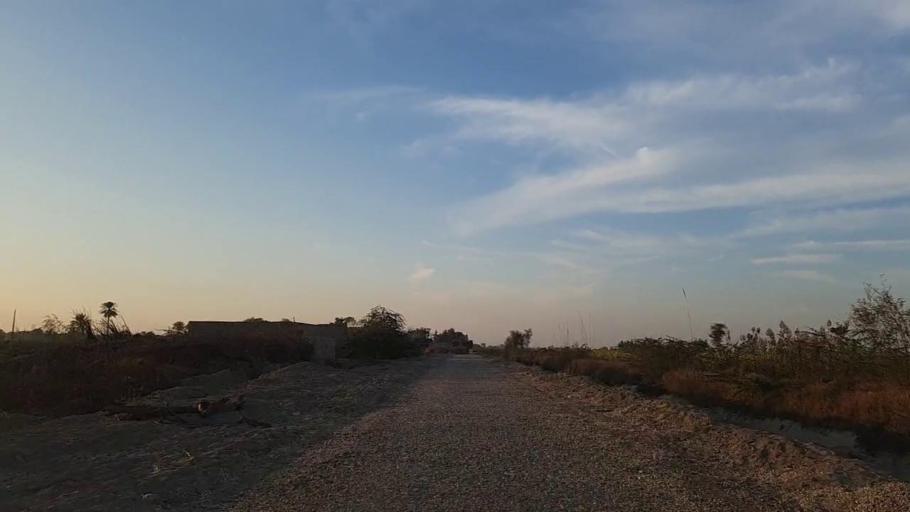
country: PK
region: Sindh
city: Bandhi
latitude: 26.6137
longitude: 68.3566
